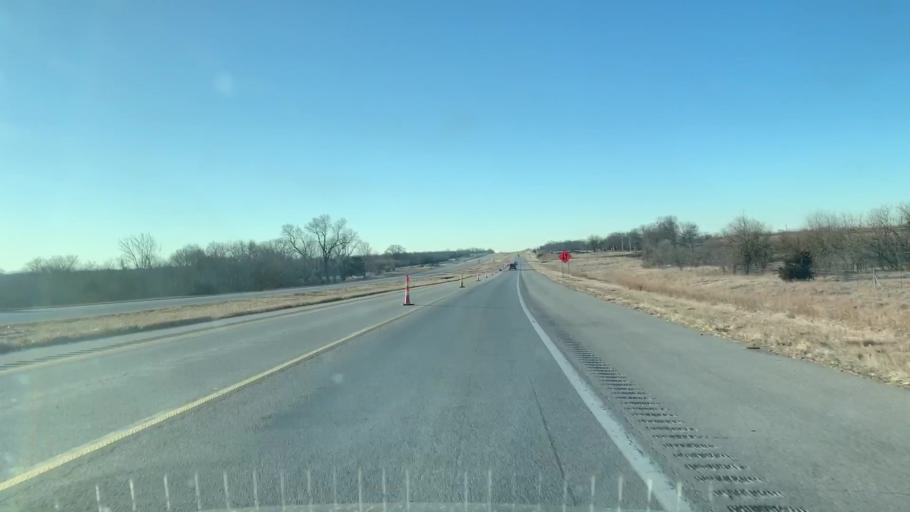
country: US
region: Kansas
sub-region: Bourbon County
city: Fort Scott
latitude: 37.7649
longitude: -94.7049
